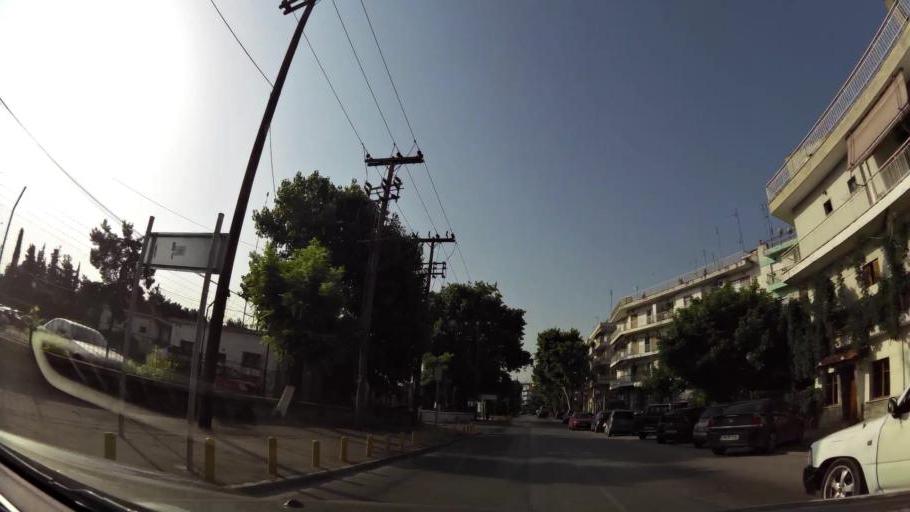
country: GR
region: Central Macedonia
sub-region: Nomos Thessalonikis
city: Evosmos
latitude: 40.6592
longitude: 22.9129
